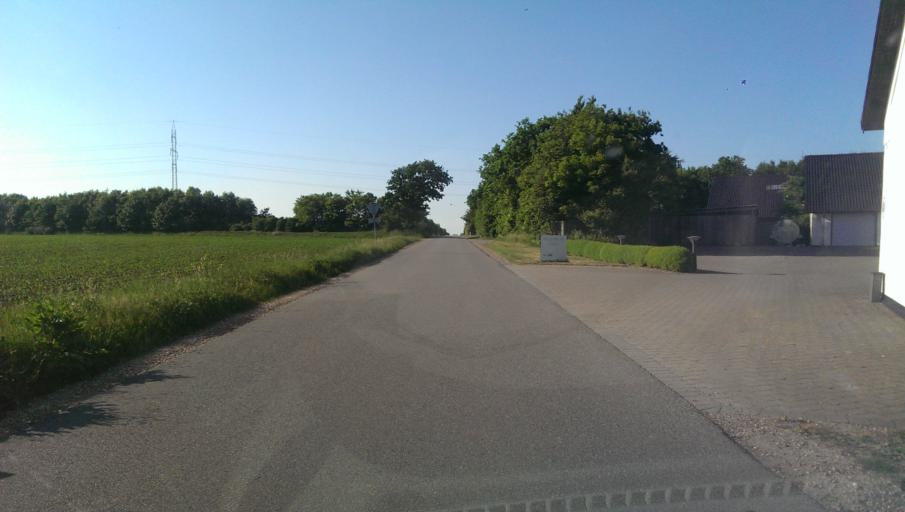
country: DK
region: South Denmark
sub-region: Esbjerg Kommune
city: Bramming
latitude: 55.5258
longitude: 8.6940
